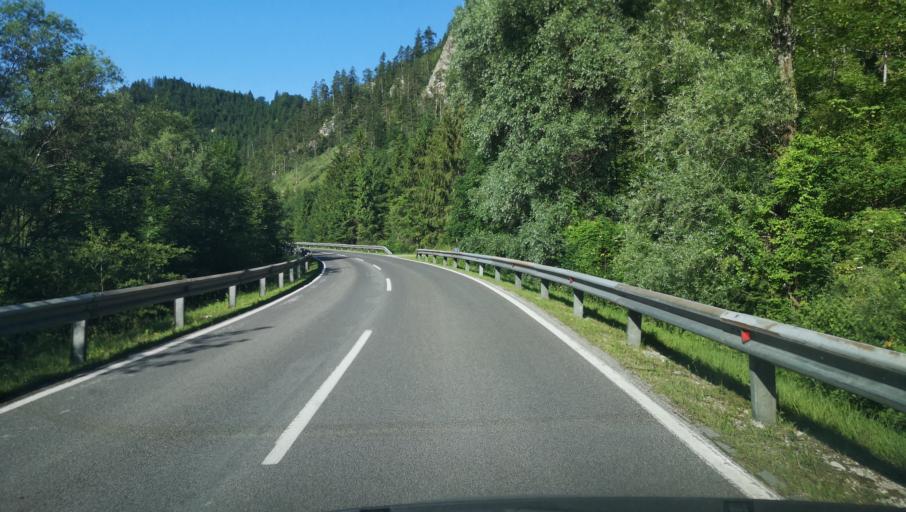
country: AT
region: Lower Austria
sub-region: Politischer Bezirk Amstetten
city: Opponitz
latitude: 47.8711
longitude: 14.7931
